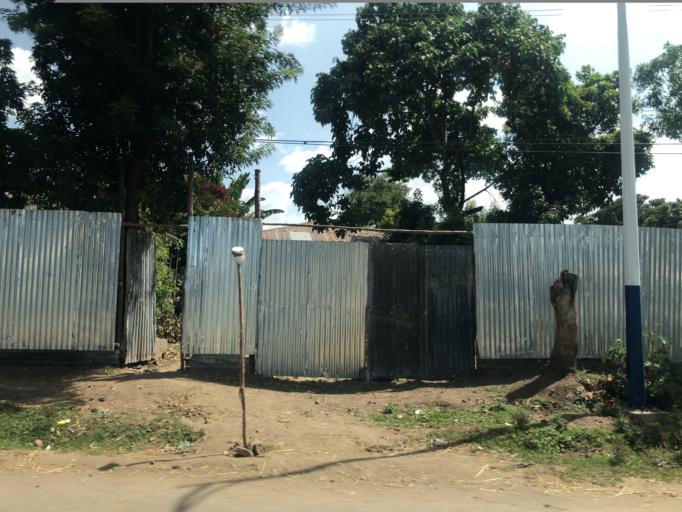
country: ET
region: Oromiya
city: Shashemene
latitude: 7.2189
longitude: 38.6237
